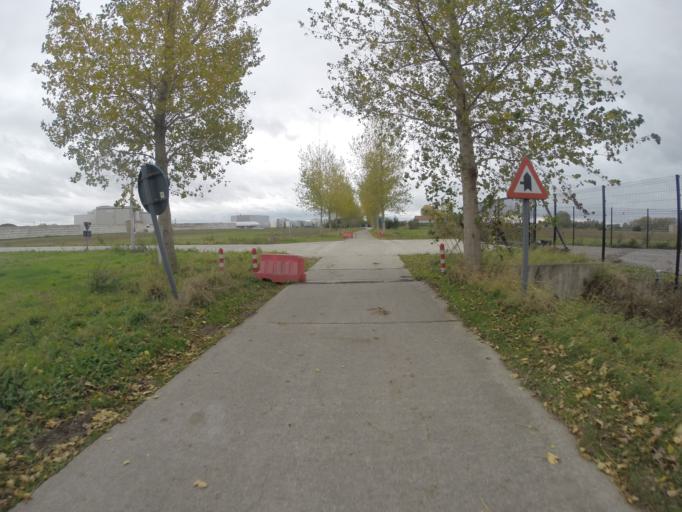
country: BE
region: Flanders
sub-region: Provincie Oost-Vlaanderen
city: Aalter
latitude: 51.1139
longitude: 3.4483
